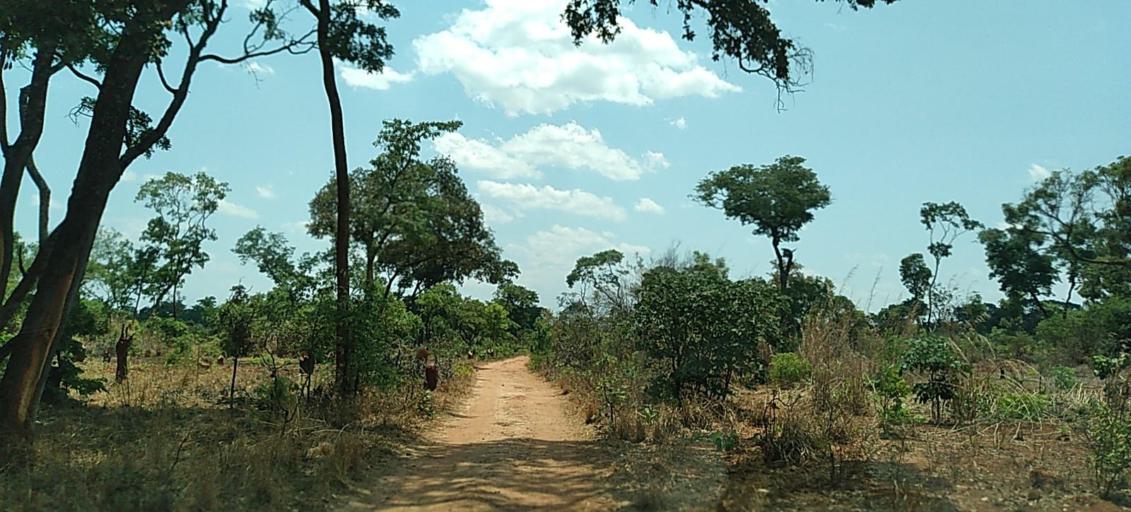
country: ZM
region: Central
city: Kapiri Mposhi
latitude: -13.6311
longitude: 28.7674
